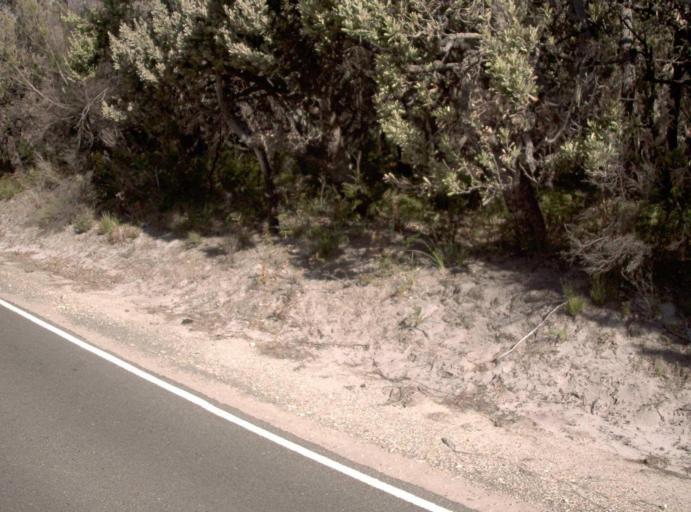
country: AU
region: Victoria
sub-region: East Gippsland
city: Lakes Entrance
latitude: -37.8012
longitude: 148.7302
